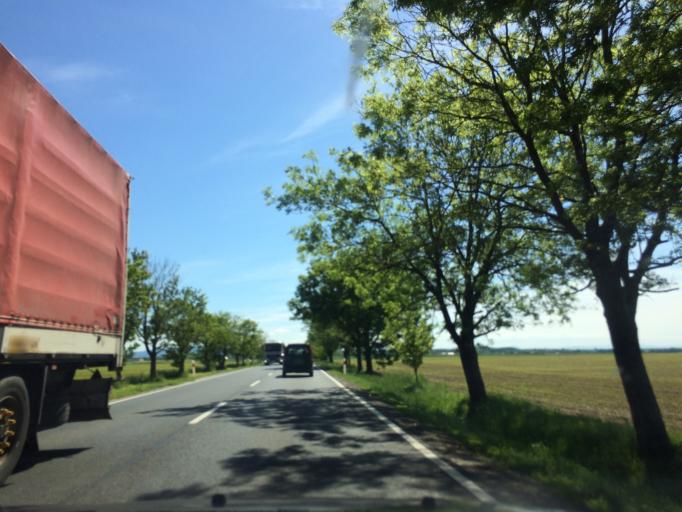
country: PL
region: Lower Silesian Voivodeship
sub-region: Powiat wroclawski
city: Gniechowice
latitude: 51.0036
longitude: 16.8552
